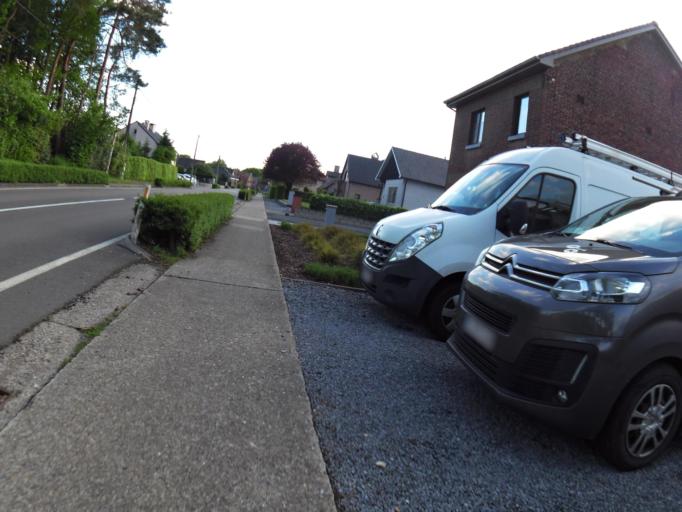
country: BE
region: Flanders
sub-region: Provincie Limburg
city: Zutendaal
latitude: 50.9381
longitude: 5.5887
